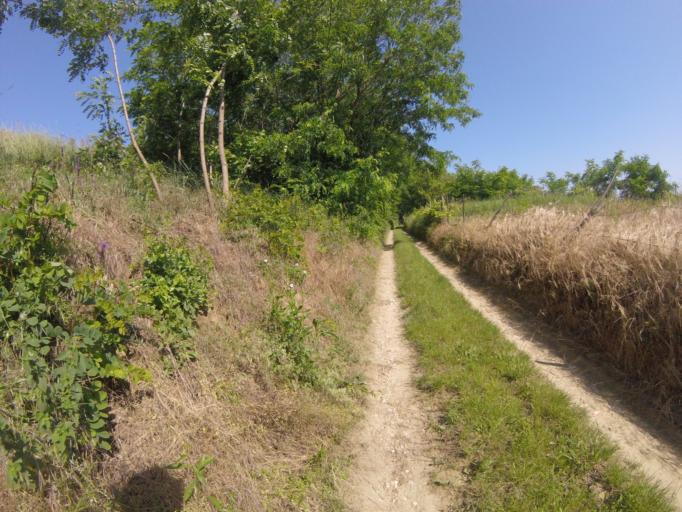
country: HU
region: Zala
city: Zalaszentgrot
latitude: 46.8984
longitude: 17.0673
